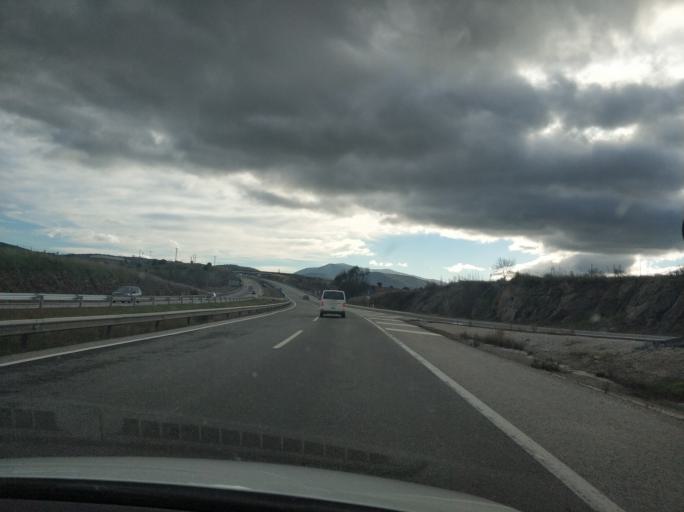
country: ES
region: Madrid
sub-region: Provincia de Madrid
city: Buitrago del Lozoya
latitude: 40.9969
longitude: -3.6416
